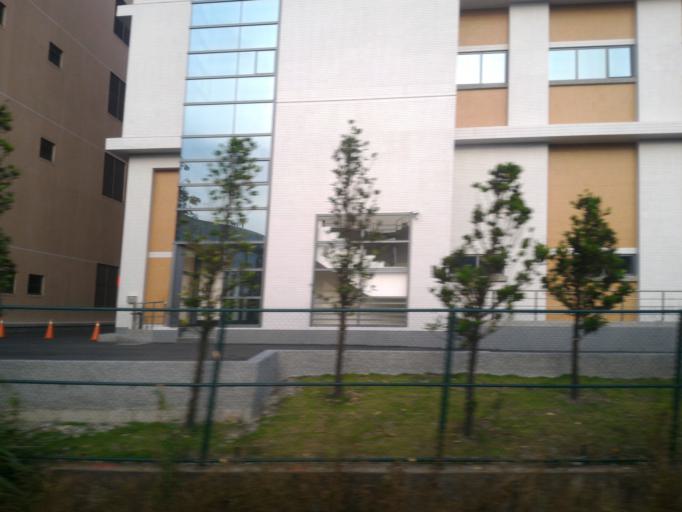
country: TW
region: Taiwan
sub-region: Taoyuan
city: Taoyuan
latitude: 24.9845
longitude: 121.3260
